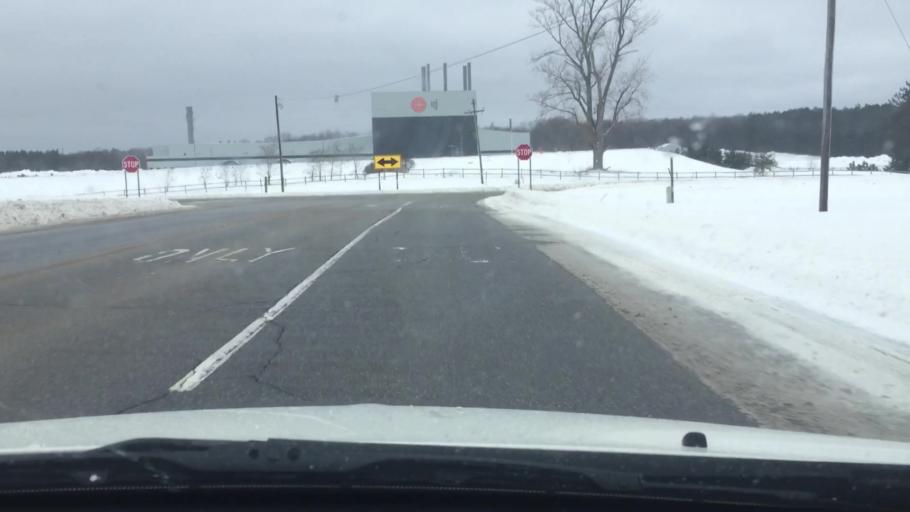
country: US
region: Michigan
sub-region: Charlevoix County
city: Boyne City
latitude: 45.0666
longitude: -84.8970
